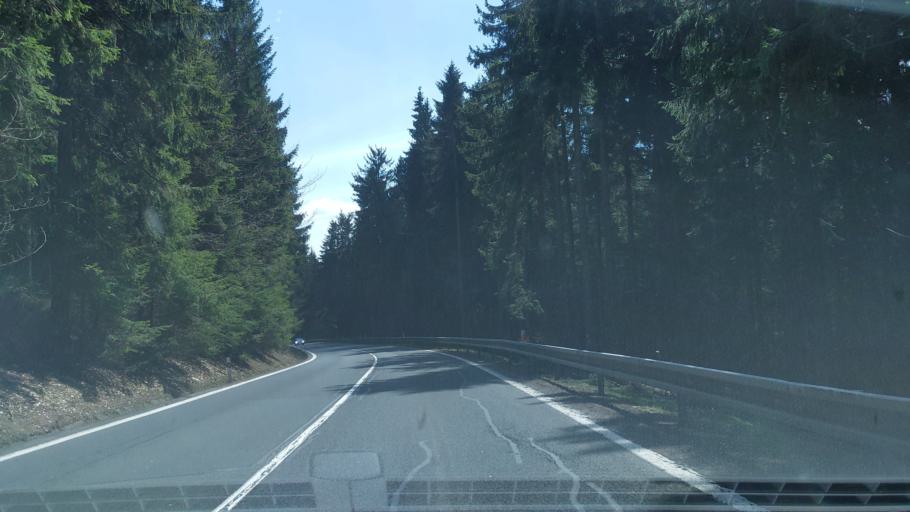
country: CZ
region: Karlovarsky
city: Jachymov
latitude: 50.3878
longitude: 12.9095
